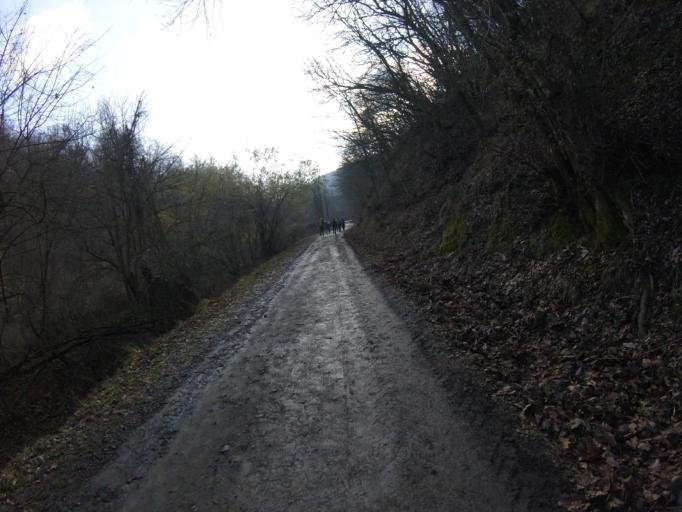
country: HU
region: Komarom-Esztergom
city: Pilismarot
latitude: 47.7461
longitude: 18.9020
